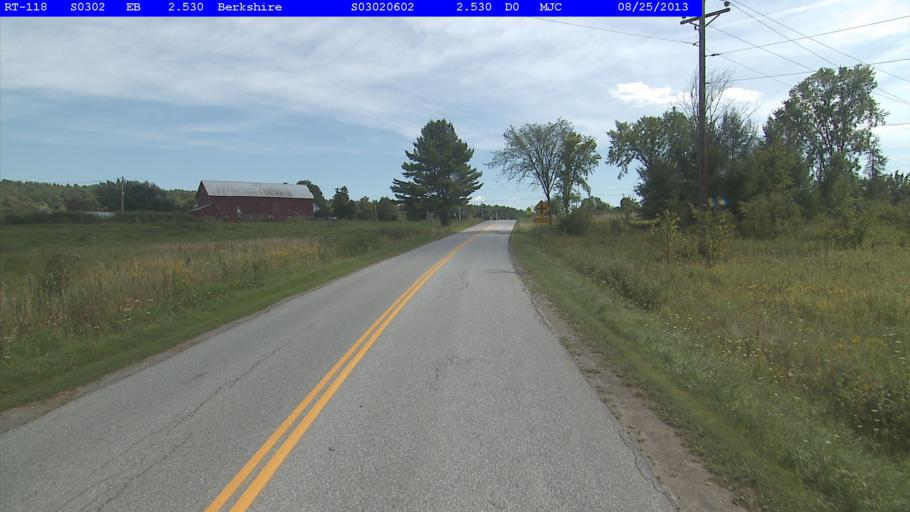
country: US
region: Vermont
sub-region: Franklin County
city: Enosburg Falls
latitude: 44.9744
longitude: -72.7676
